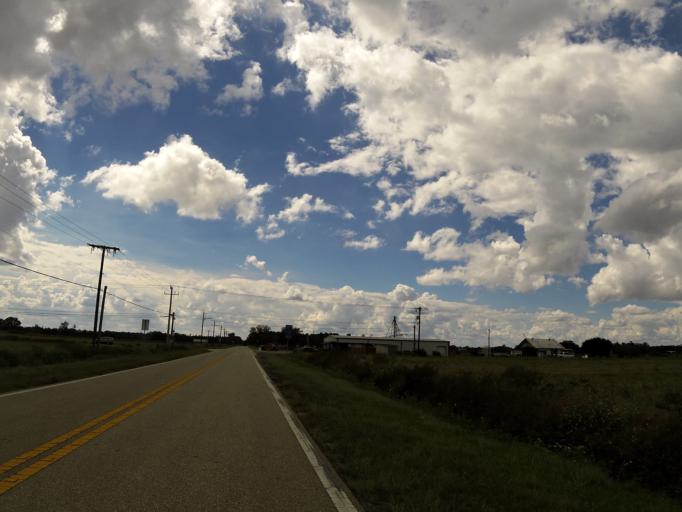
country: US
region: Florida
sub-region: Saint Johns County
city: Saint Augustine South
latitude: 29.8513
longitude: -81.4975
